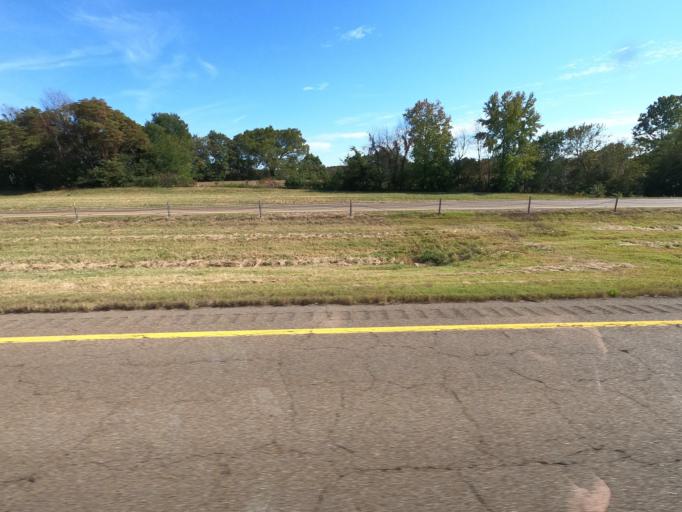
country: US
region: Tennessee
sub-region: Obion County
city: Union City
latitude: 36.4561
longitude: -88.9978
